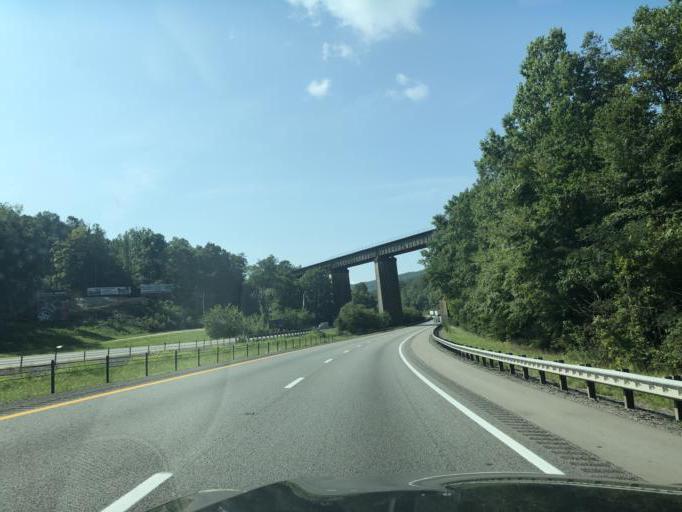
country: US
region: Georgia
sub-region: Dade County
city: Trenton
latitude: 35.0026
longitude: -85.5124
